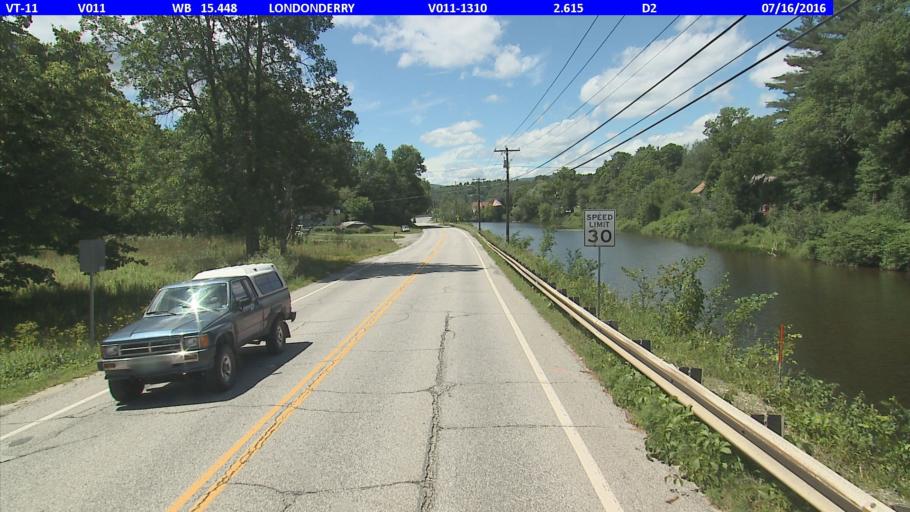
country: US
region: Vermont
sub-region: Windsor County
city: Chester
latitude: 43.2258
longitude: -72.8028
